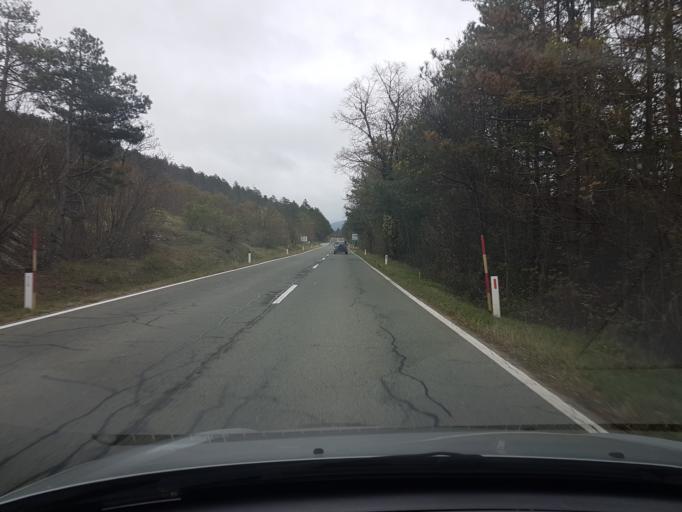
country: SI
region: Divaca
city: Divaca
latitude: 45.7278
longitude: 13.9713
